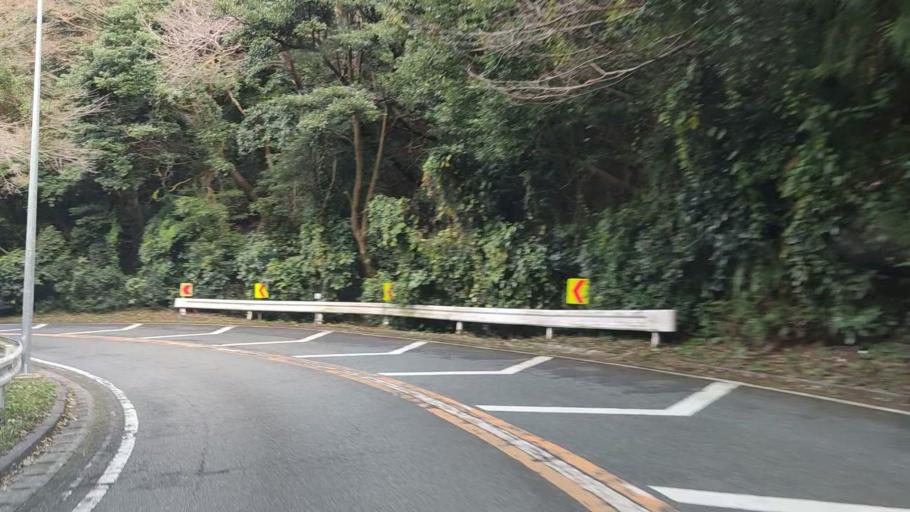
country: JP
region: Shizuoka
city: Shizuoka-shi
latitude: 34.9713
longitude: 138.4741
